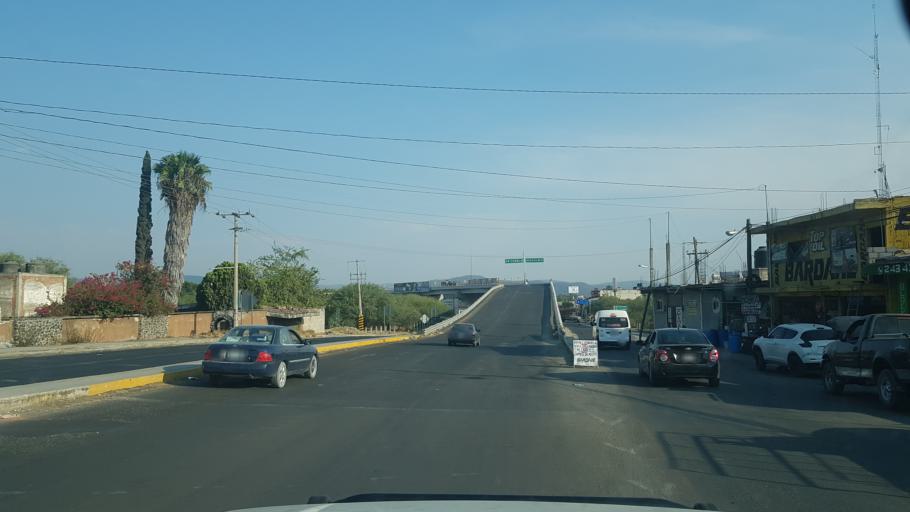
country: MX
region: Puebla
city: Izucar de Matamoros
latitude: 18.6017
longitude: -98.4816
